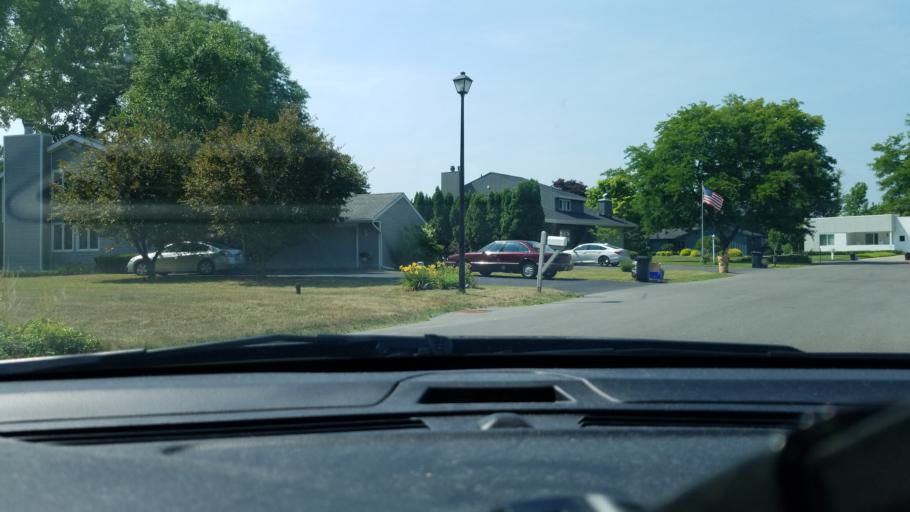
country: US
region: New York
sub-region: Onondaga County
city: Liverpool
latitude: 43.1098
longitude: -76.2227
